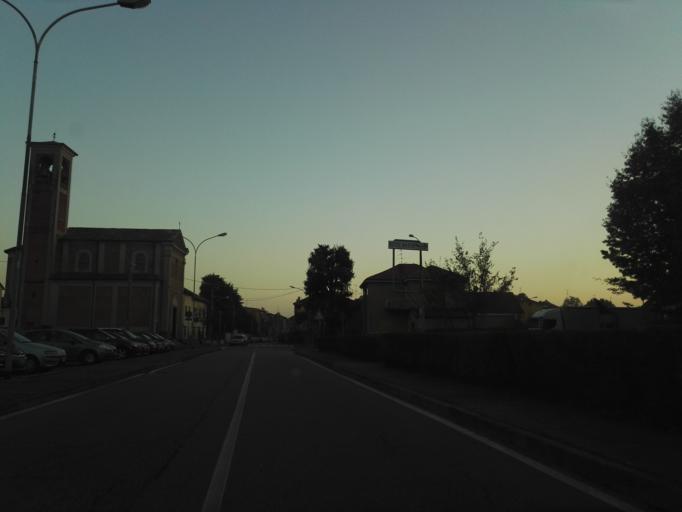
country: IT
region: Lombardy
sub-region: Citta metropolitana di Milano
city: Mezzate
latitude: 45.4473
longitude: 9.2935
